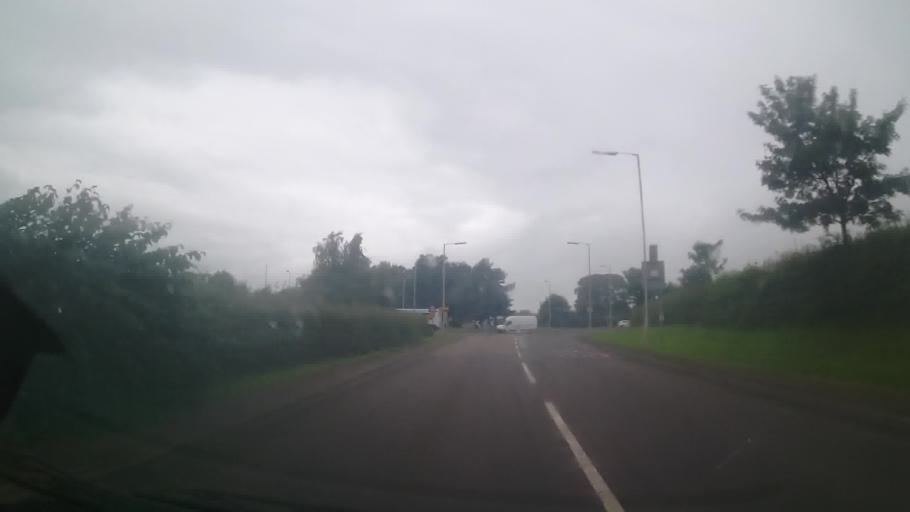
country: GB
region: England
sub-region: Shropshire
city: Whitchurch
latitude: 52.9570
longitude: -2.6739
